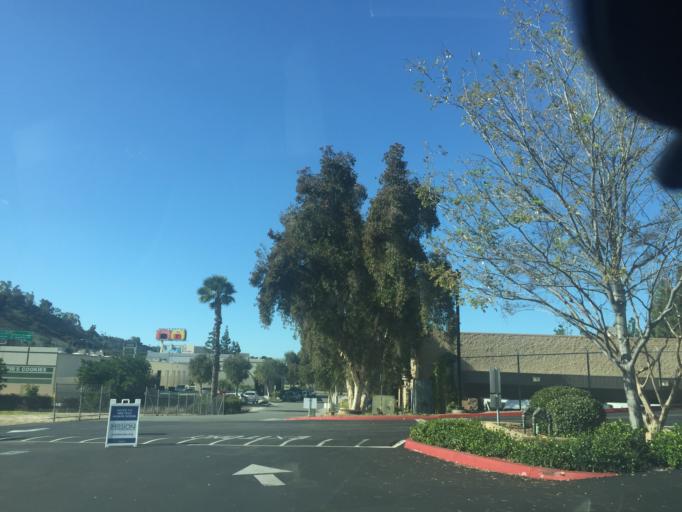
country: US
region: California
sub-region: San Diego County
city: La Mesa
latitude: 32.7818
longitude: -117.0899
